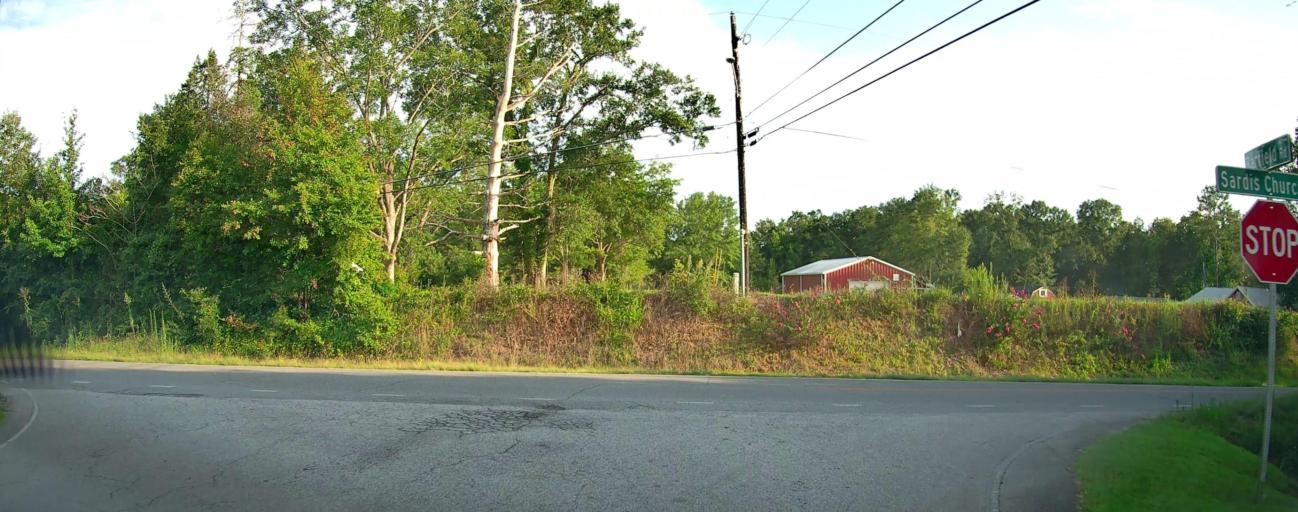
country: US
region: Georgia
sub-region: Peach County
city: Byron
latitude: 32.7181
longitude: -83.7469
